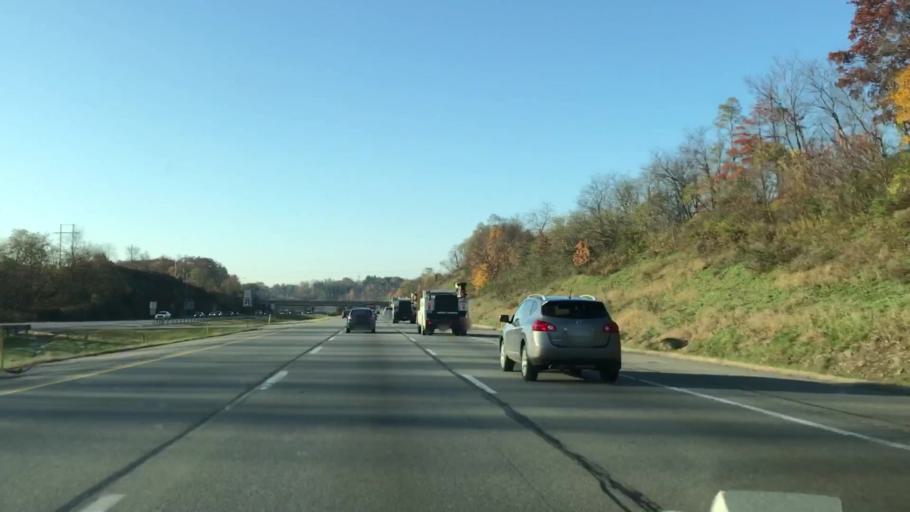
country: US
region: Pennsylvania
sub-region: Allegheny County
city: Franklin Park
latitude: 40.5935
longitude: -80.0959
